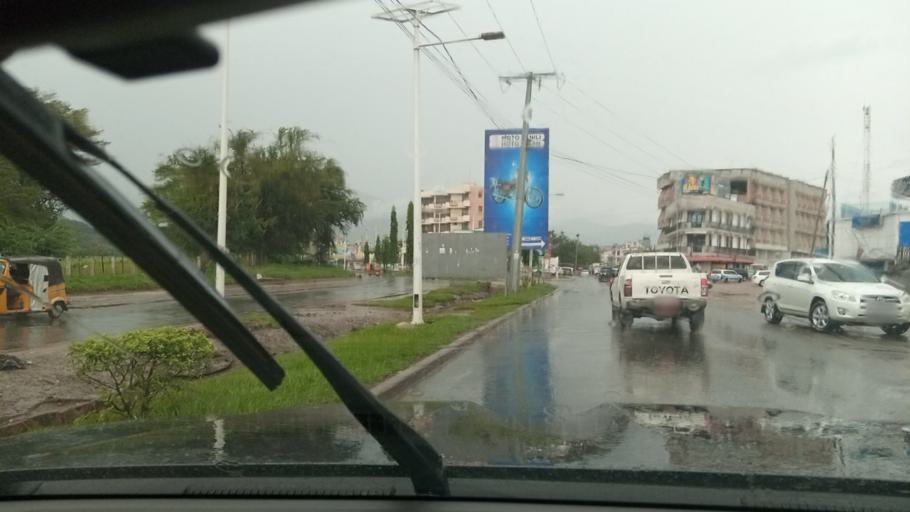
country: BI
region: Bujumbura Mairie
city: Bujumbura
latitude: -3.3783
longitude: 29.3531
